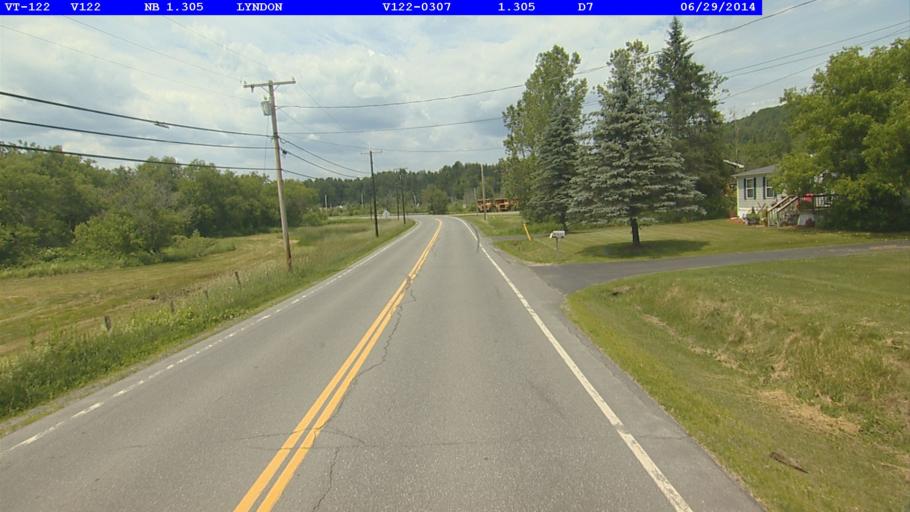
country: US
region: Vermont
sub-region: Caledonia County
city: Lyndonville
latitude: 44.5492
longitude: -72.0216
